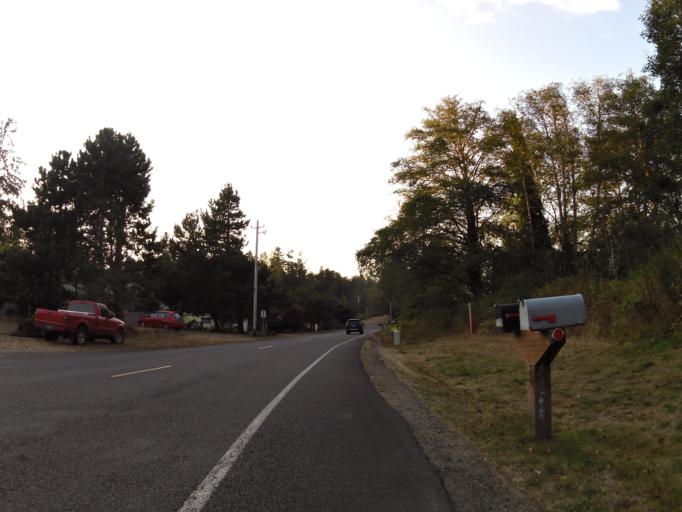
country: US
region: Oregon
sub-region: Clatsop County
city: Warrenton
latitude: 46.1586
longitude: -123.9444
